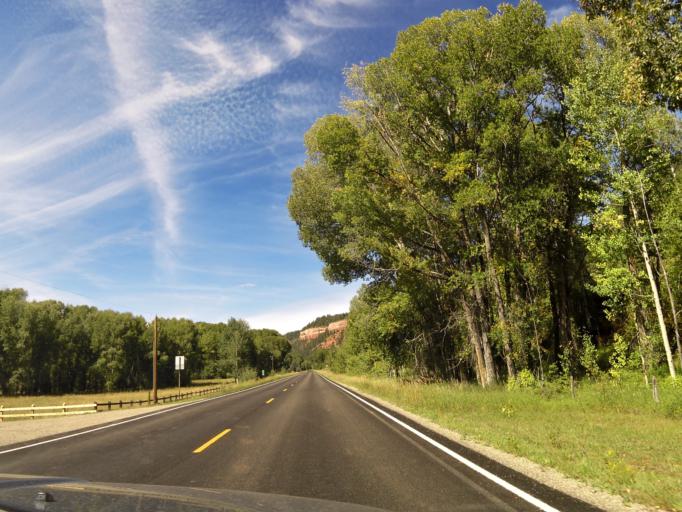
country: US
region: Colorado
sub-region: Montezuma County
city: Mancos
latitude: 37.5783
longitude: -108.2202
